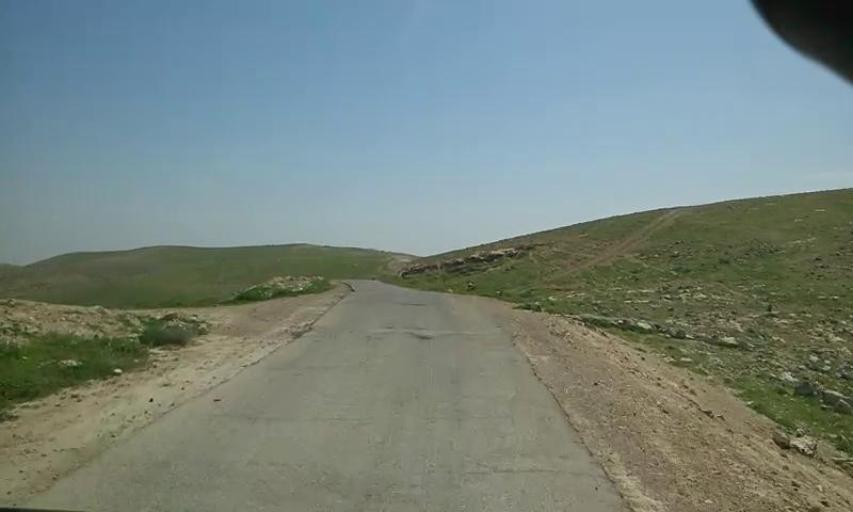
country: PS
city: `Arab ar Rashaydah
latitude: 31.5600
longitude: 35.2455
